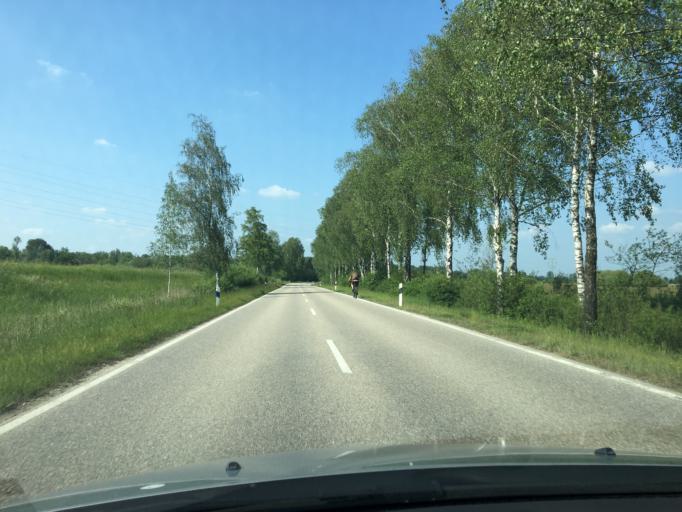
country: DE
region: Bavaria
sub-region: Upper Bavaria
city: Langenpreising
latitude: 48.4317
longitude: 11.9355
